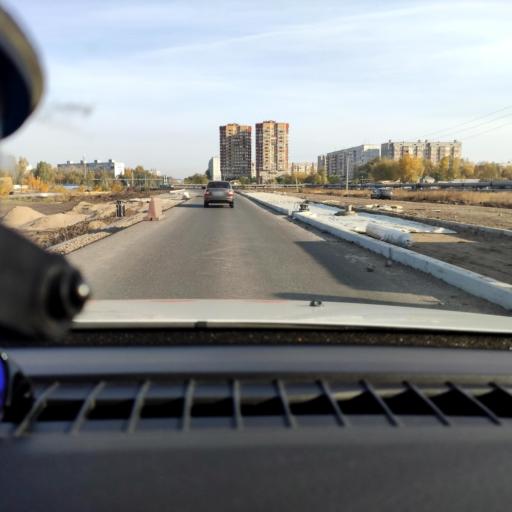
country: RU
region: Samara
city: Samara
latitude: 53.1027
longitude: 50.0780
